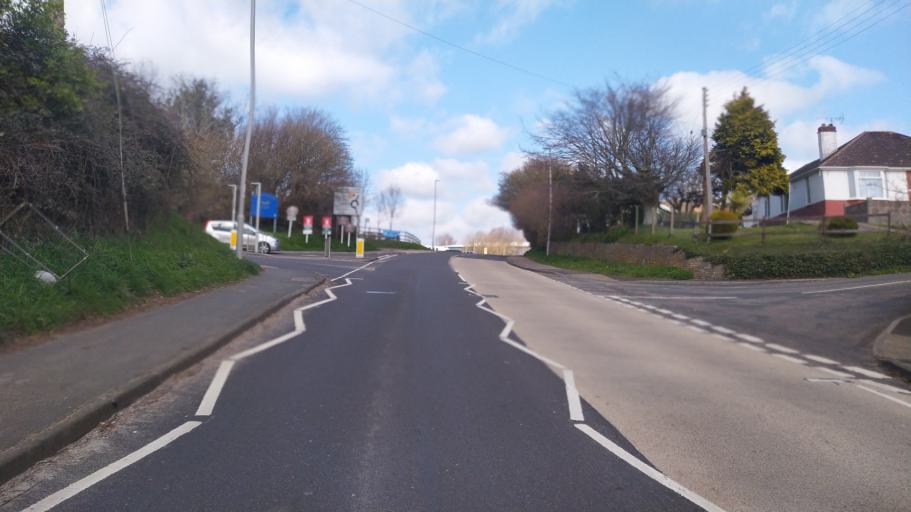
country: GB
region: England
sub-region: Dorset
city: Bridport
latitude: 50.7466
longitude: -2.7427
